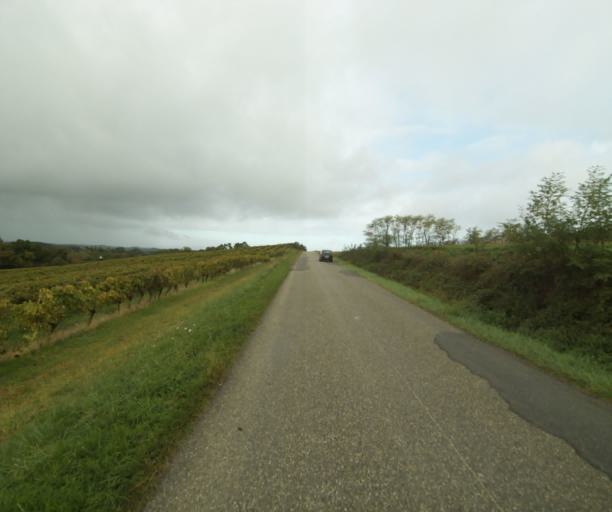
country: FR
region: Midi-Pyrenees
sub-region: Departement du Gers
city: Nogaro
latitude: 43.8282
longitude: -0.0387
